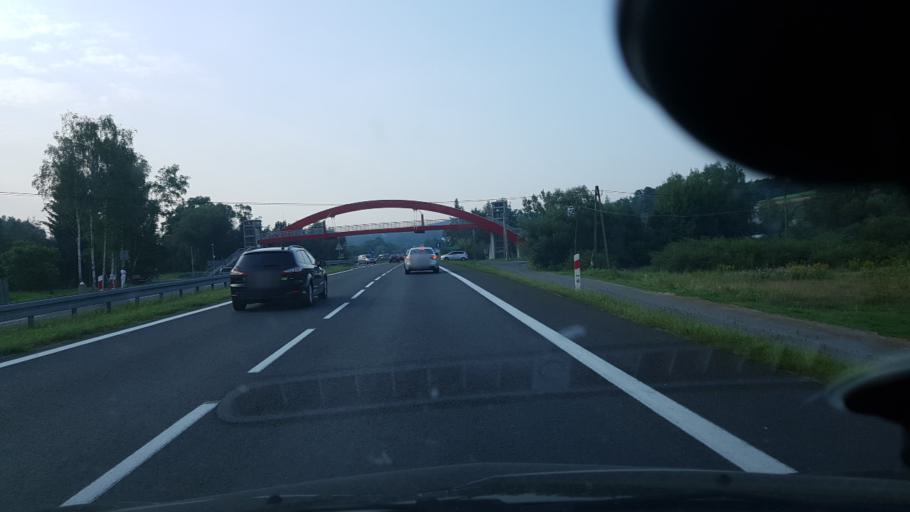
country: PL
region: Lesser Poland Voivodeship
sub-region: Powiat myslenicki
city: Glogoczow
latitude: 49.9024
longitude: 19.8710
